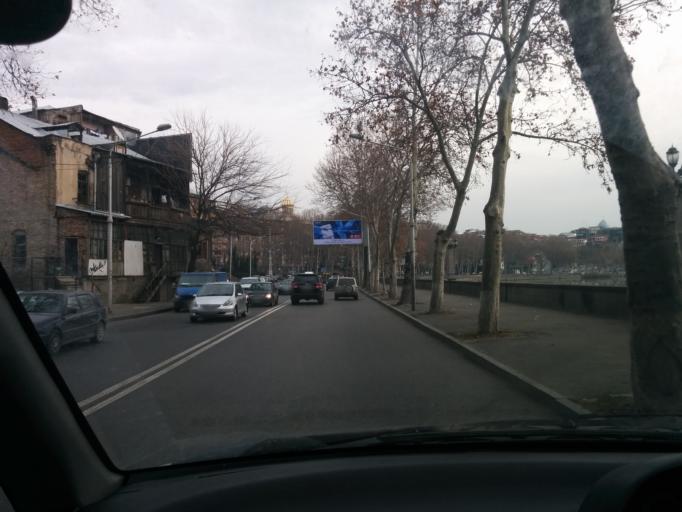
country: GE
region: T'bilisi
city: Tbilisi
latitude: 41.7019
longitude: 44.8055
